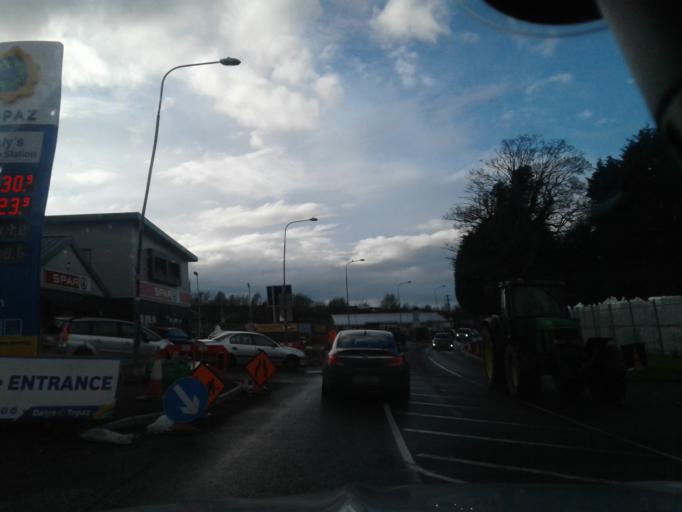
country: IE
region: Ulster
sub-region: County Donegal
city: Leifear
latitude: 54.8335
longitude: -7.4872
